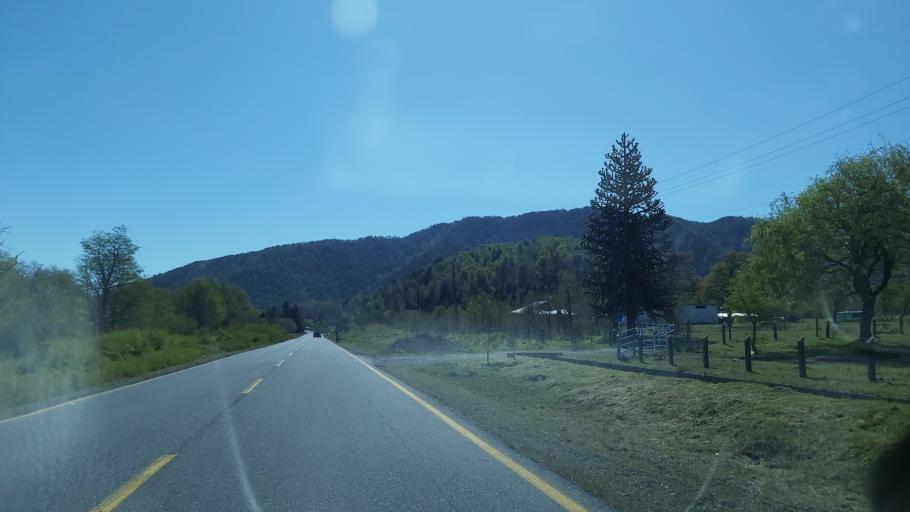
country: CL
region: Araucania
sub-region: Provincia de Cautin
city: Vilcun
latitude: -38.4642
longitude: -71.6118
